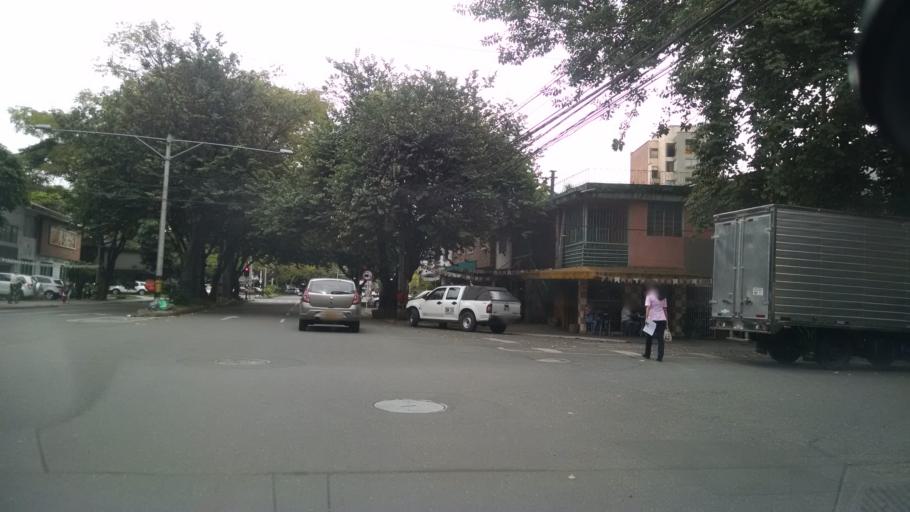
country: CO
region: Antioquia
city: Medellin
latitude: 6.2448
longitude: -75.5916
